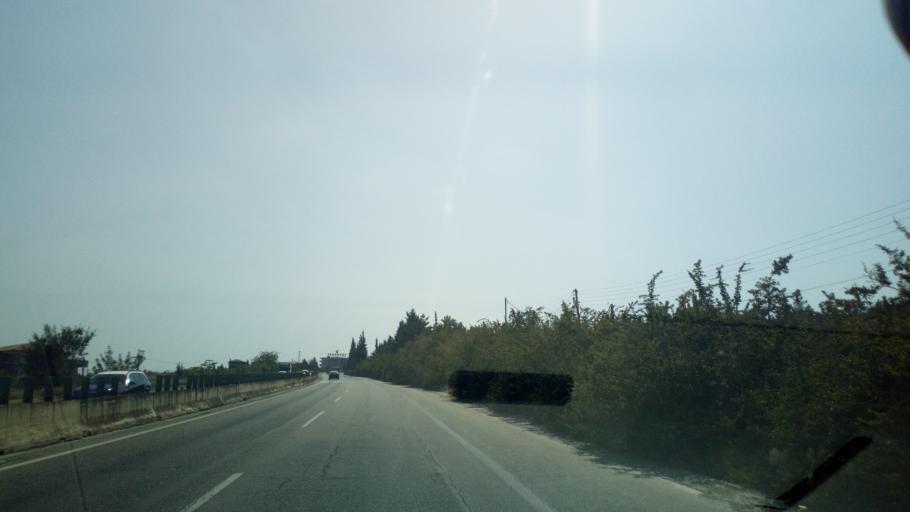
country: GR
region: Central Macedonia
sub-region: Nomos Thessalonikis
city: Neo Rysi
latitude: 40.4915
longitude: 22.9988
